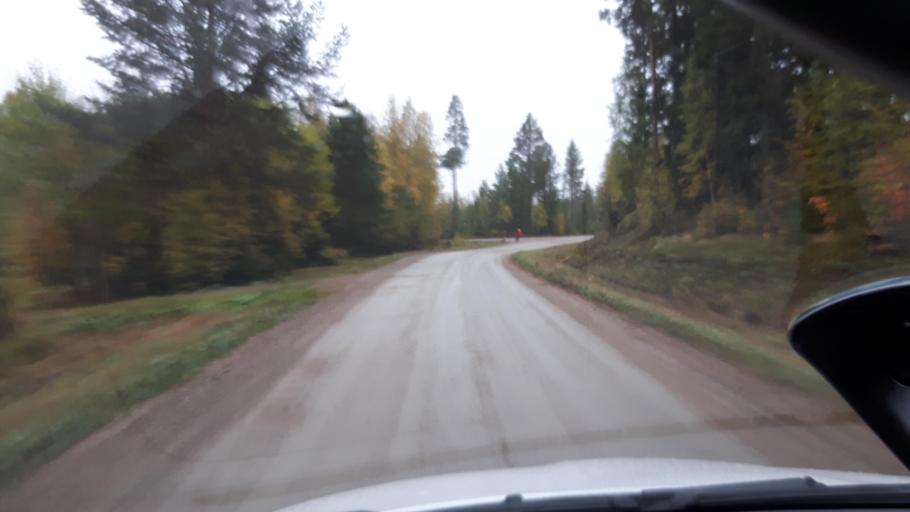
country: SE
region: Vaesternorrland
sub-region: Ange Kommun
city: Ange
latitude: 62.1430
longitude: 15.6617
